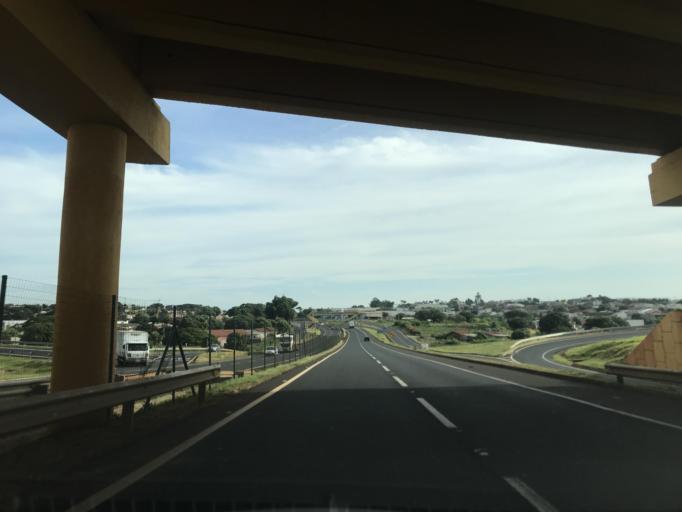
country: BR
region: Parana
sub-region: Mandaguacu
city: Mandaguacu
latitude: -23.3497
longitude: -52.0909
